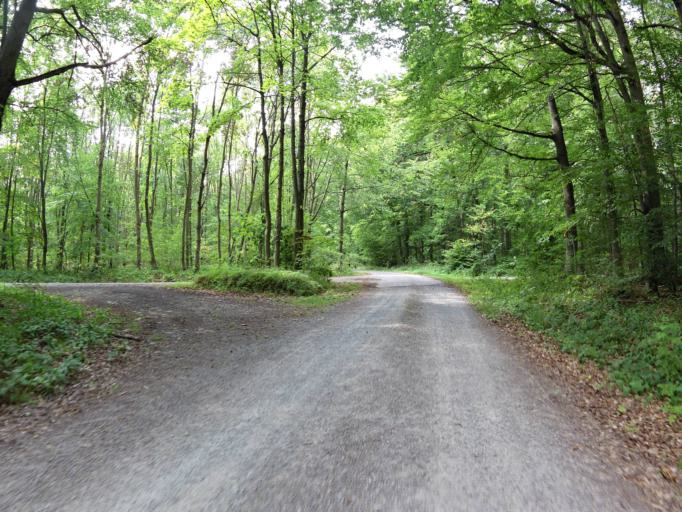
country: DE
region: Bavaria
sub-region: Regierungsbezirk Unterfranken
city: Kleinrinderfeld
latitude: 49.7079
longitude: 9.8149
